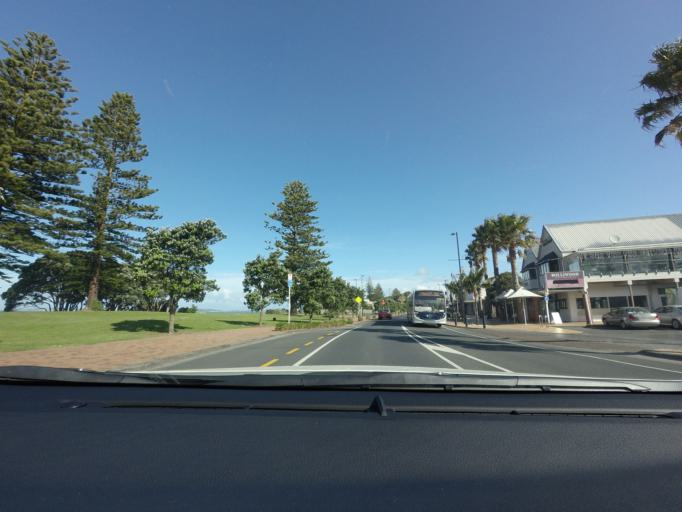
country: NZ
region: Auckland
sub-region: Auckland
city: Rothesay Bay
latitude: -36.5857
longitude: 174.6959
